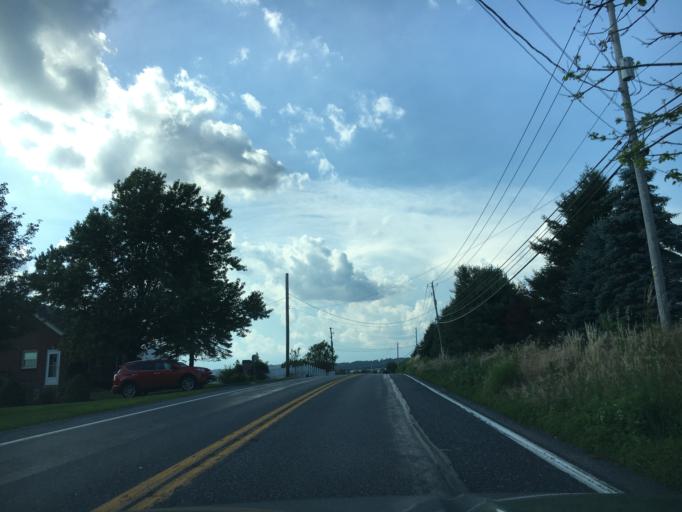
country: US
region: Pennsylvania
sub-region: Lehigh County
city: Schnecksville
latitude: 40.6879
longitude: -75.5869
